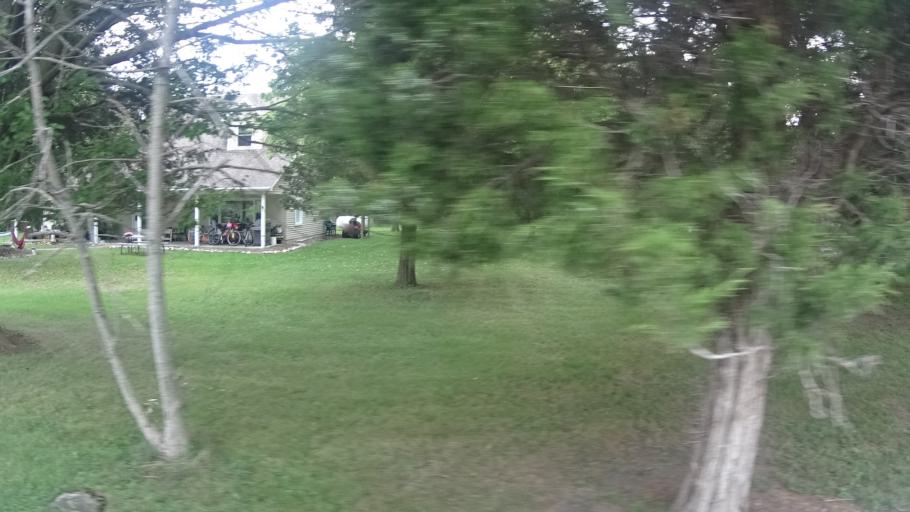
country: US
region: Ohio
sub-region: Erie County
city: Sandusky
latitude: 41.6051
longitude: -82.6867
